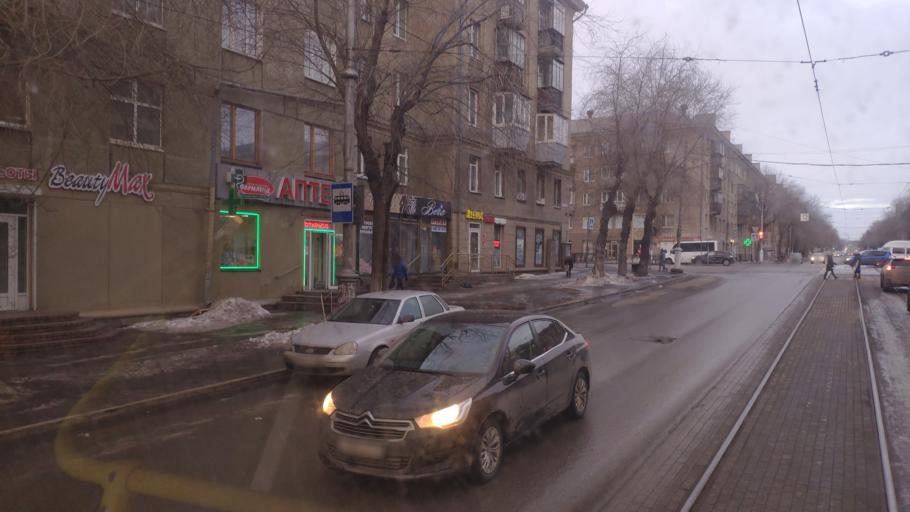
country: RU
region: Chelyabinsk
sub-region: Gorod Magnitogorsk
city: Magnitogorsk
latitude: 53.4178
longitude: 58.9854
